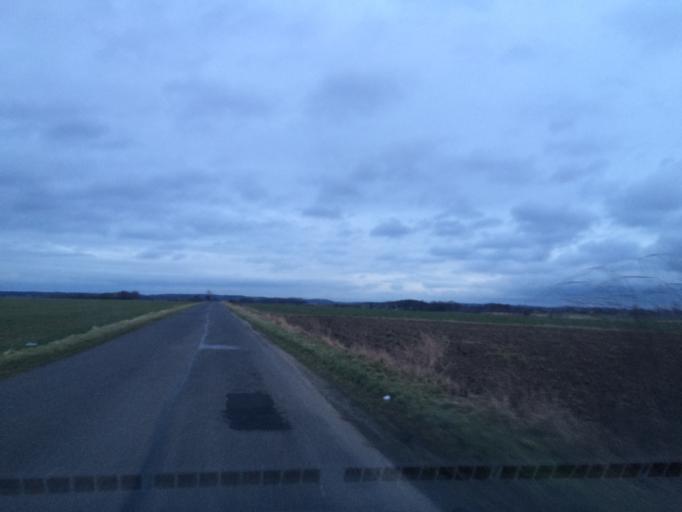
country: PL
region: Lower Silesian Voivodeship
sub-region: Powiat boleslawiecki
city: Nowogrodziec
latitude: 51.1989
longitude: 15.4708
